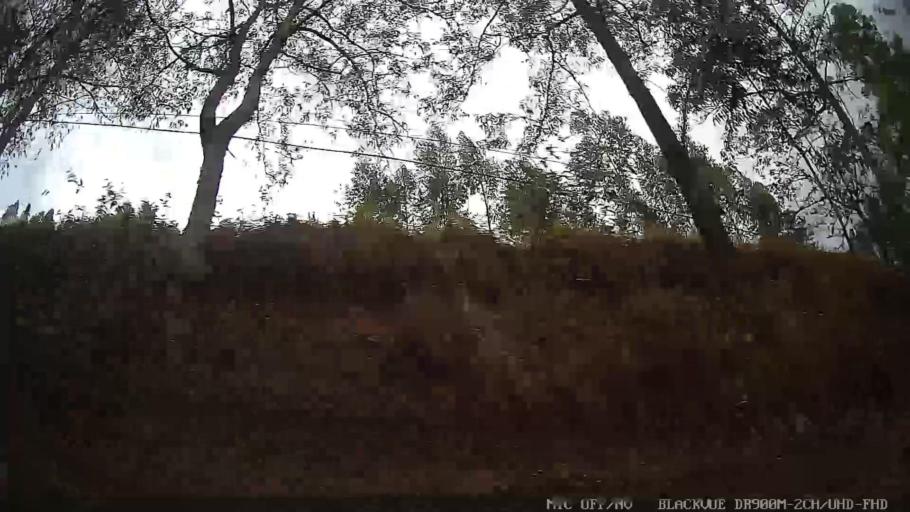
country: BR
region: Sao Paulo
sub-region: Itatiba
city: Itatiba
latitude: -23.0021
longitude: -46.8779
